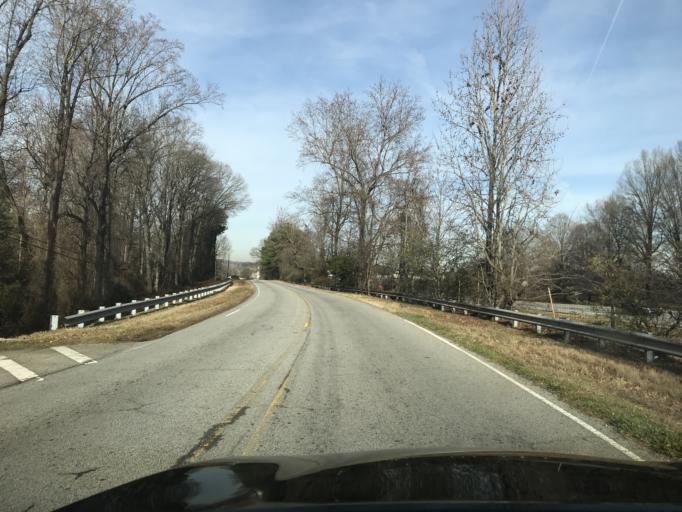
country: US
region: Georgia
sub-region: Clayton County
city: Riverdale
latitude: 33.5843
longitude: -84.3798
